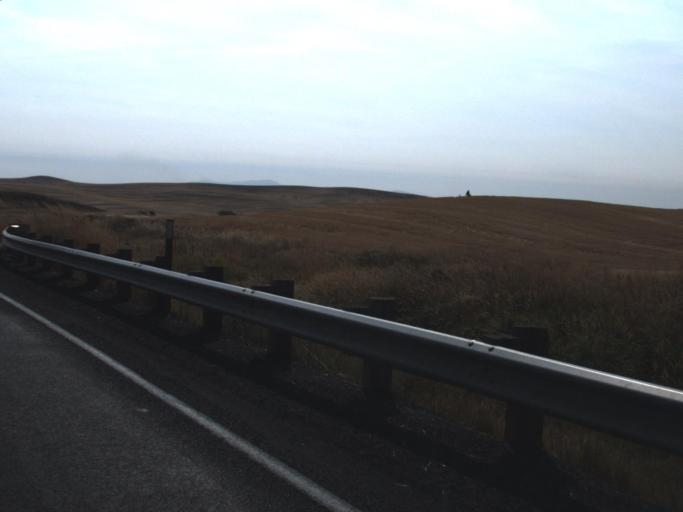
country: US
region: Washington
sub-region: Whitman County
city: Pullman
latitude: 46.9807
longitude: -117.1241
